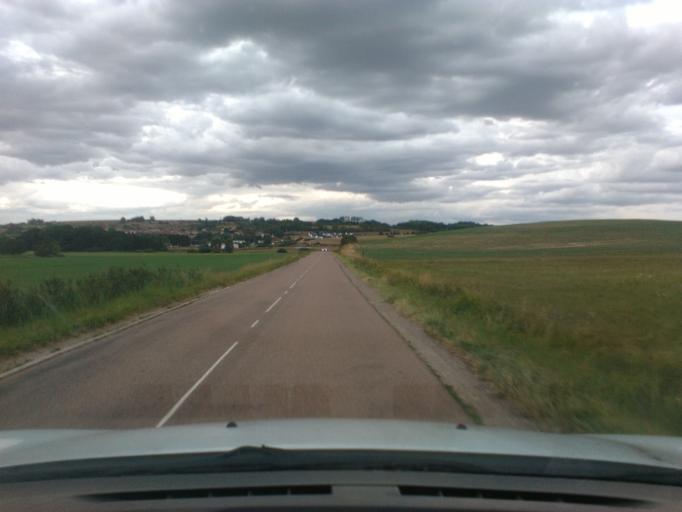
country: FR
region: Lorraine
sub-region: Departement des Vosges
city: Charmes
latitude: 48.3576
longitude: 6.2671
